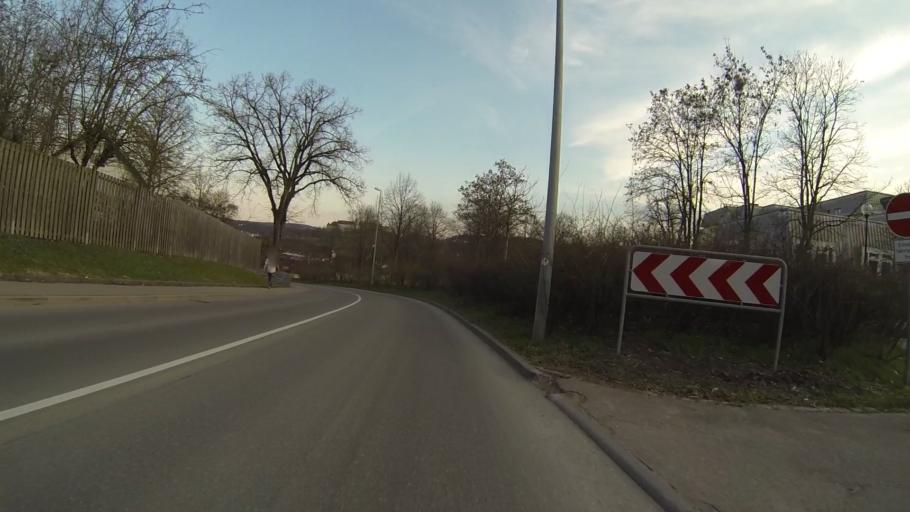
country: DE
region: Baden-Wuerttemberg
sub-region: Regierungsbezirk Stuttgart
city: Heidenheim an der Brenz
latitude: 48.6840
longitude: 10.1446
